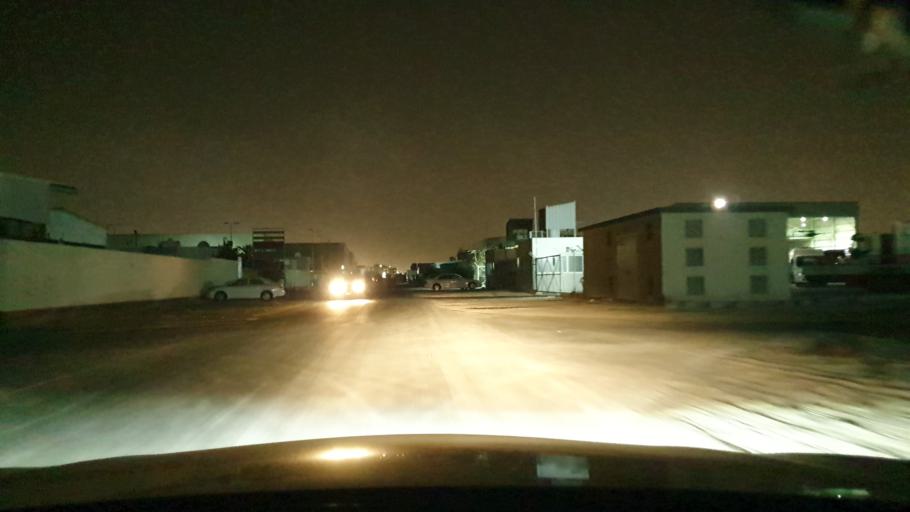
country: BH
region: Northern
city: Sitrah
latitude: 26.0973
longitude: 50.6226
